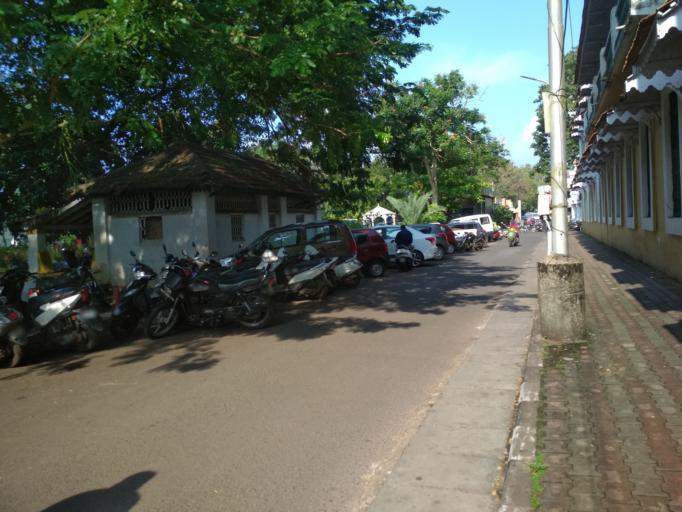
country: IN
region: Goa
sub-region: North Goa
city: Panaji
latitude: 15.5006
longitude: 73.8247
